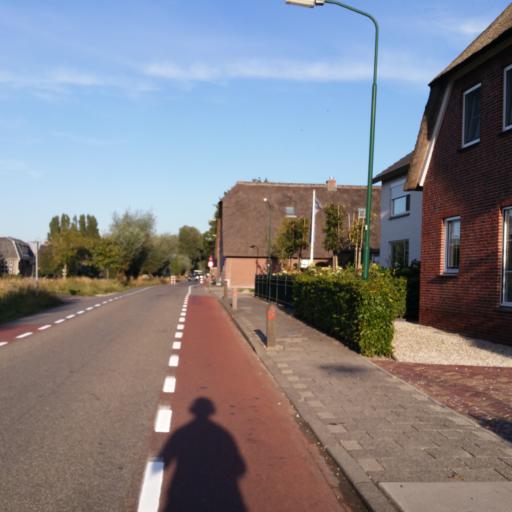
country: NL
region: Utrecht
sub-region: Gemeente Lopik
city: Lopik
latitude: 52.0059
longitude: 4.9639
